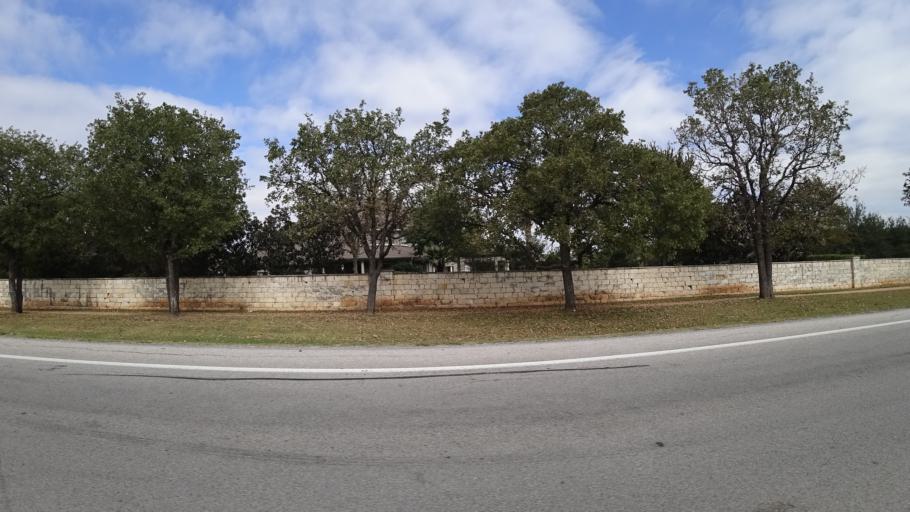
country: US
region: Texas
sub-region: Williamson County
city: Brushy Creek
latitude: 30.5321
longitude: -97.7118
